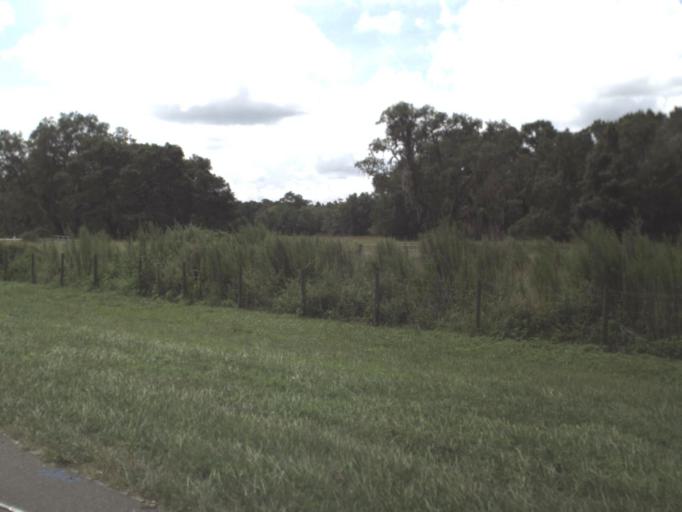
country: US
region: Florida
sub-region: Pasco County
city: Shady Hills
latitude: 28.3289
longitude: -82.5355
